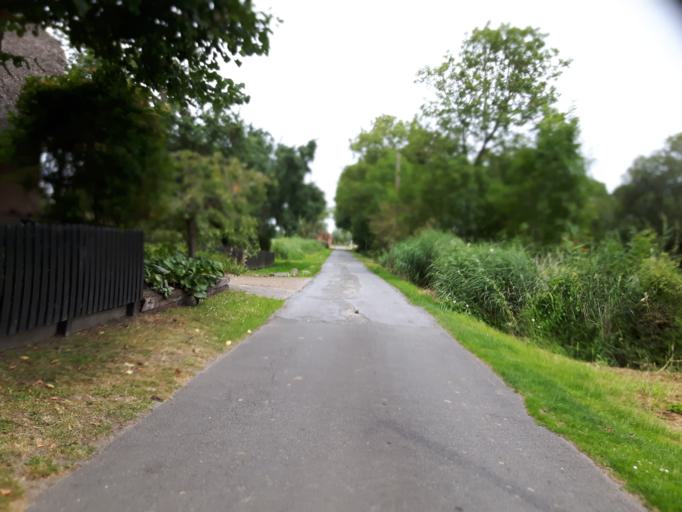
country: DE
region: Lower Saxony
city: Varel
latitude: 53.3604
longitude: 8.2050
